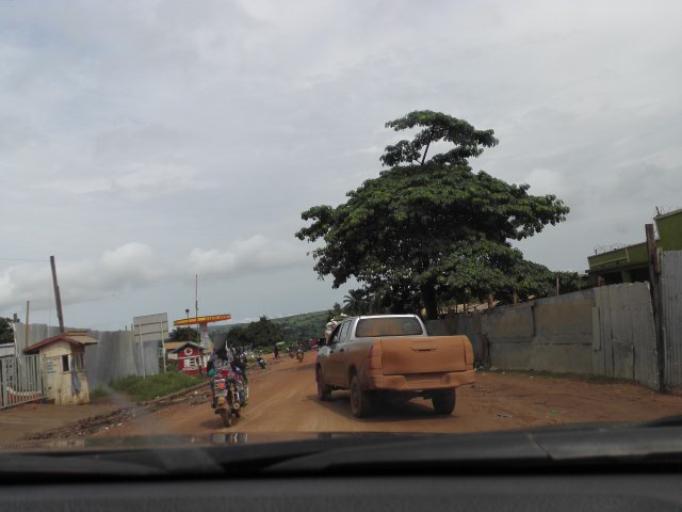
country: CD
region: Eastern Province
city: Bunia
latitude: 1.3665
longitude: 29.7633
